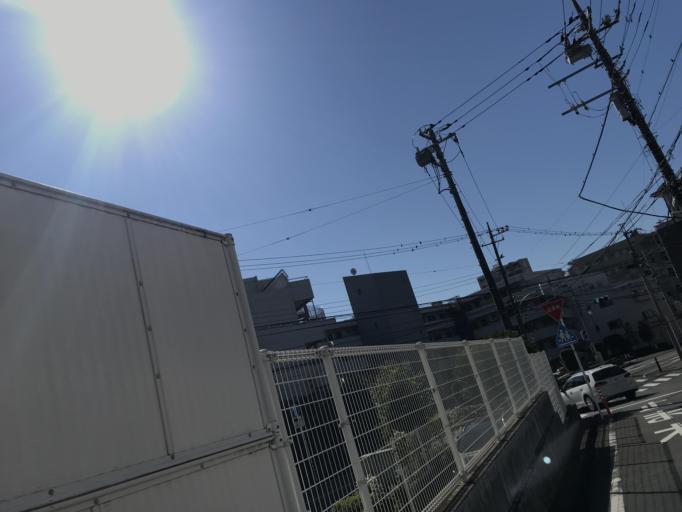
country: JP
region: Tokyo
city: Chofugaoka
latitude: 35.5795
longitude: 139.5772
